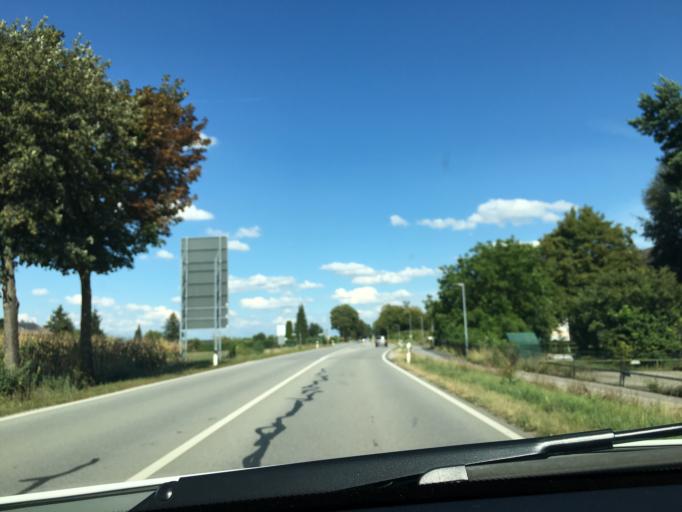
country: DE
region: Bavaria
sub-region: Lower Bavaria
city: Dingolfing
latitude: 48.6472
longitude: 12.4954
